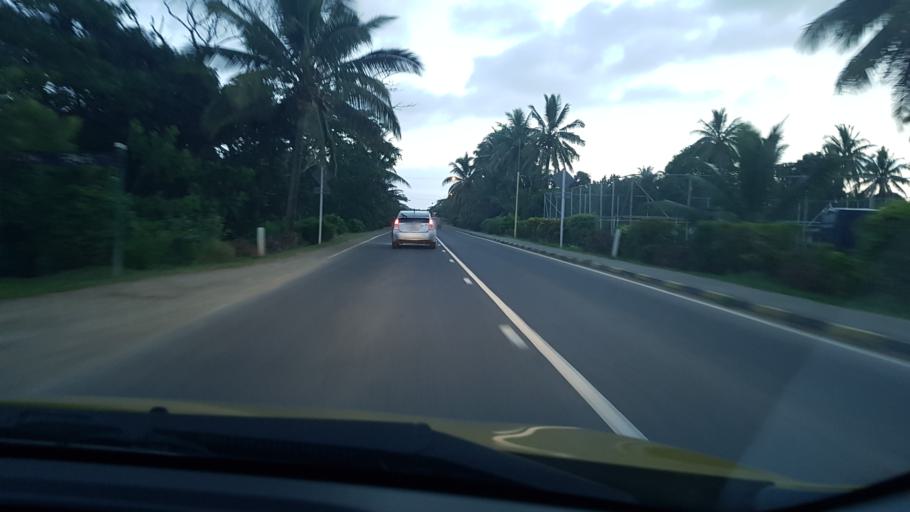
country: FJ
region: Western
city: Nadi
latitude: -18.1435
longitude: 177.5123
